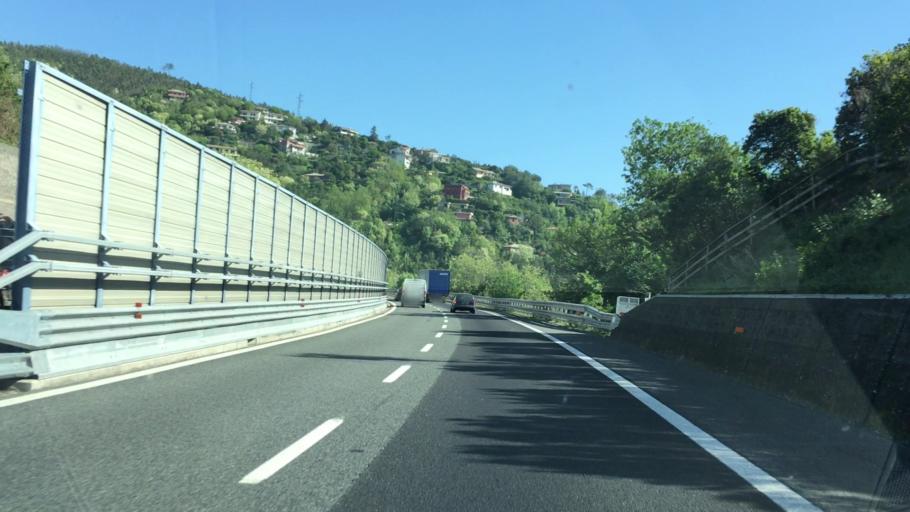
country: IT
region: Liguria
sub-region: Provincia di Genova
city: Sestri Levante
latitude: 44.2943
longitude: 9.3843
